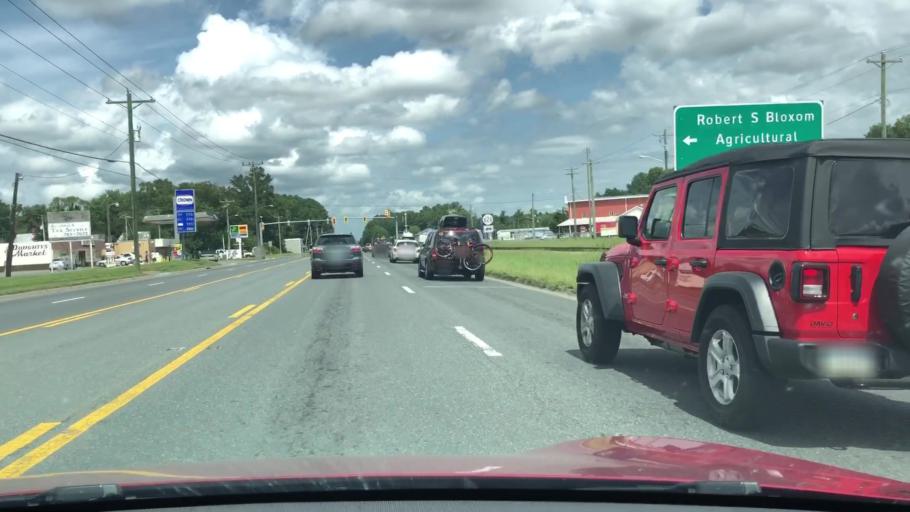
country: US
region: Virginia
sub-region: Accomack County
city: Onancock
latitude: 37.6489
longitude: -75.7431
